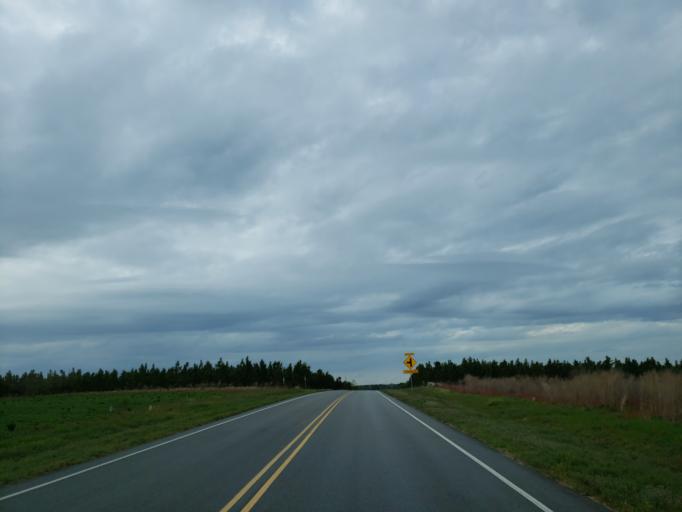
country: US
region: Georgia
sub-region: Dooly County
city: Vienna
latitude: 32.1181
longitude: -83.7560
